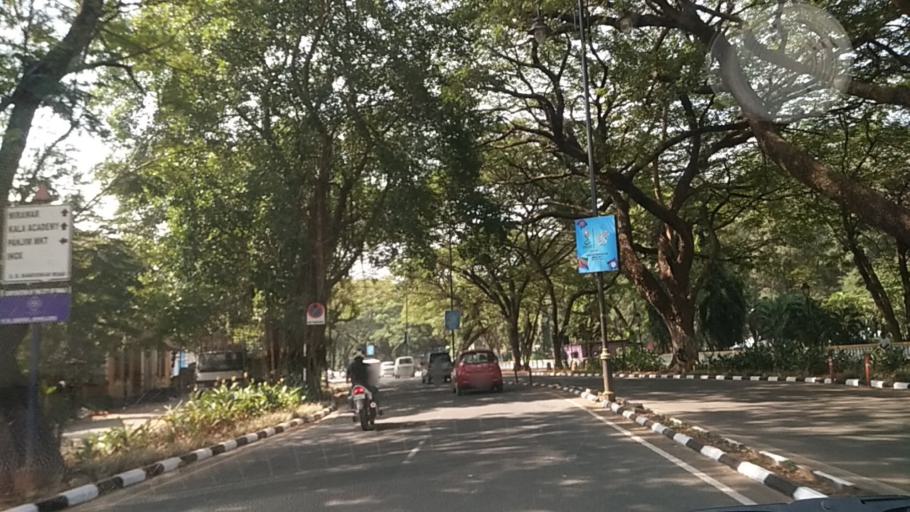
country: IN
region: Goa
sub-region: North Goa
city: Panaji
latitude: 15.4987
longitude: 73.8199
